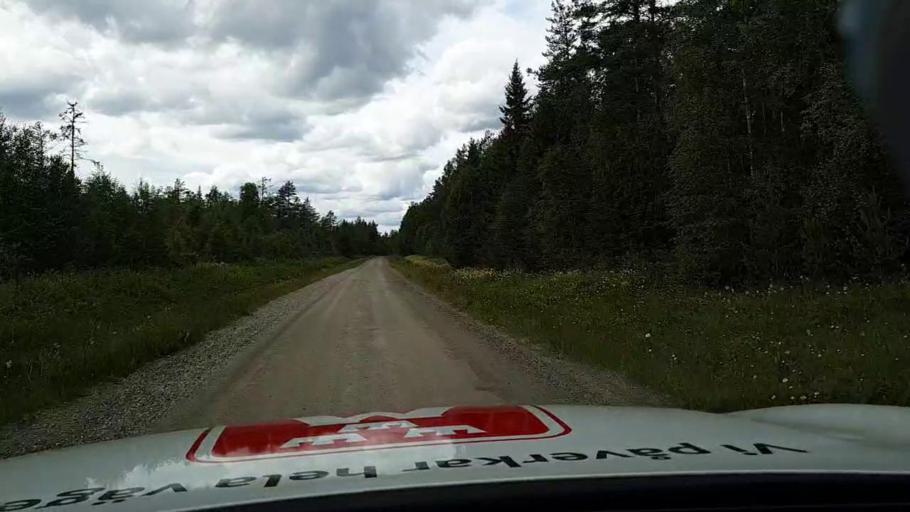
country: SE
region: Jaemtland
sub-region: Stroemsunds Kommun
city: Stroemsund
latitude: 63.3159
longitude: 15.4892
